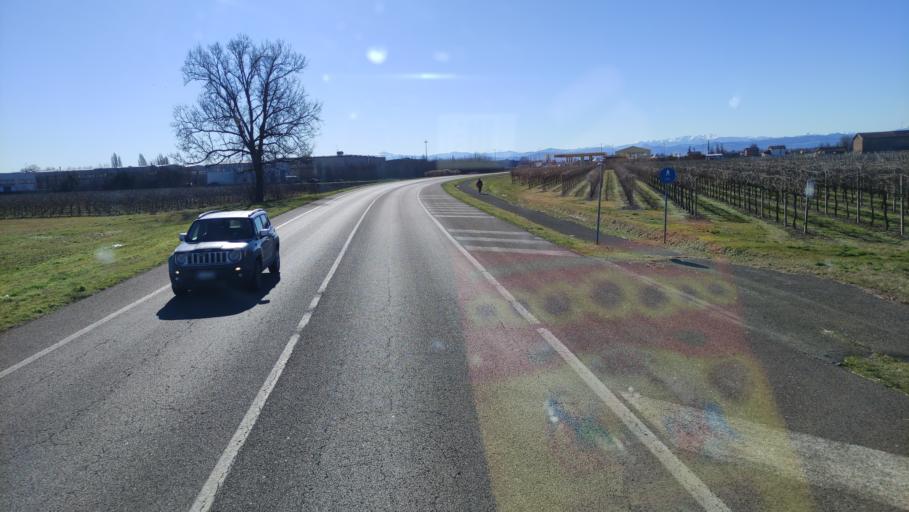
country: IT
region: Emilia-Romagna
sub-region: Provincia di Reggio Emilia
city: San Martino in Rio
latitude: 44.7301
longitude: 10.7661
